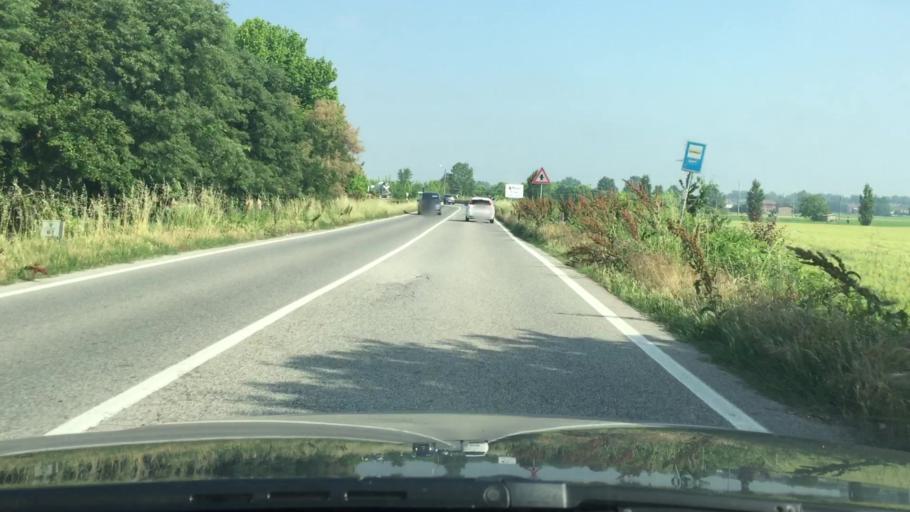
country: IT
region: Emilia-Romagna
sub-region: Provincia di Ferrara
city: Pontegradella
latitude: 44.8092
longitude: 11.6352
